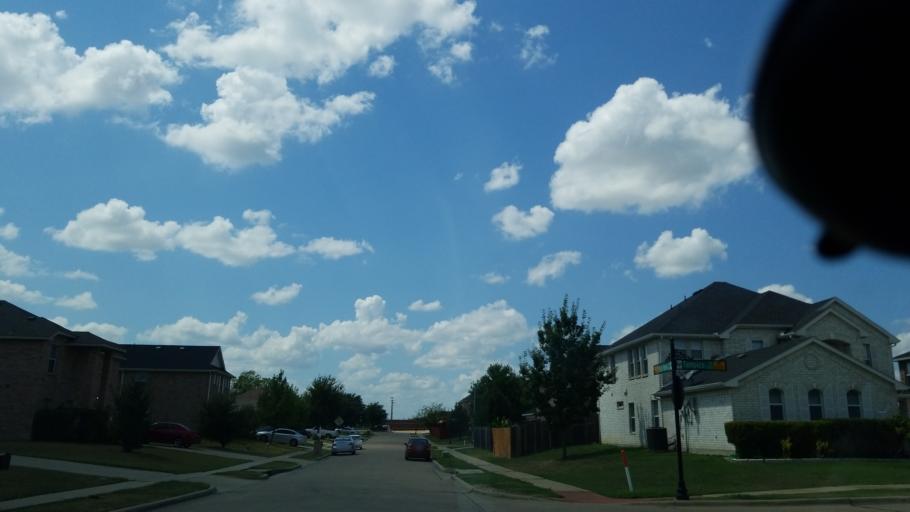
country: US
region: Texas
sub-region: Dallas County
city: Grand Prairie
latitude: 32.7251
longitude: -96.9966
